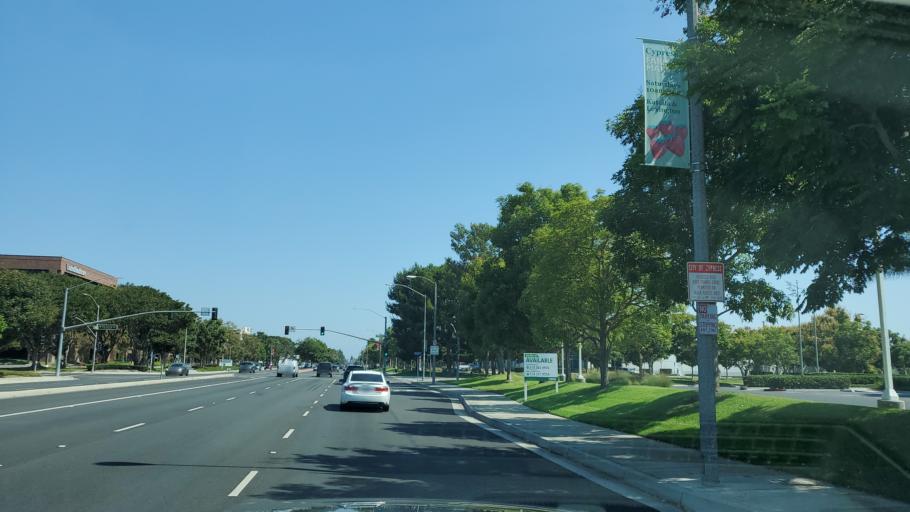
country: US
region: California
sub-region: Orange County
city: Cypress
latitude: 33.8029
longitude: -118.0355
